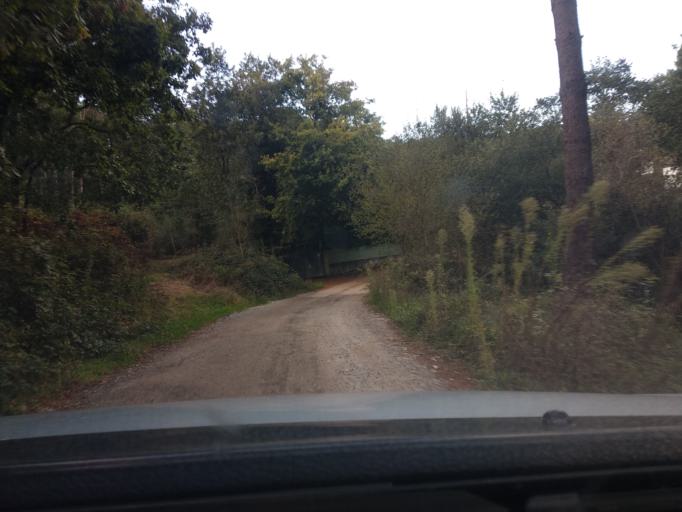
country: ES
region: Galicia
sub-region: Provincia de Pontevedra
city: Moana
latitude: 42.2969
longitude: -8.6927
